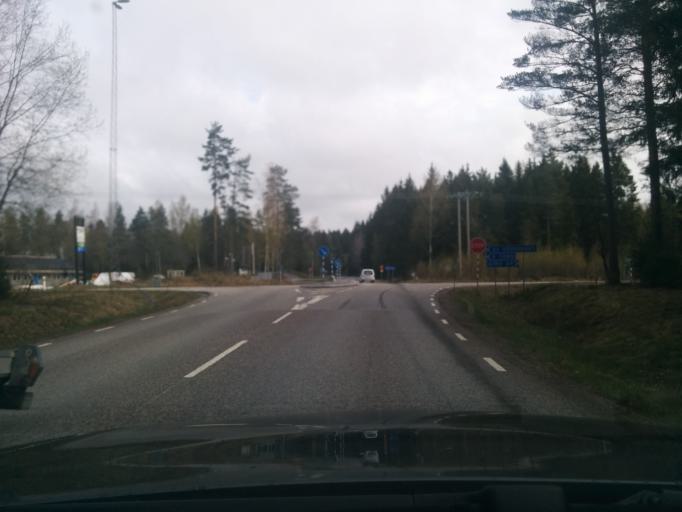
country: SE
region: Uppsala
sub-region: Tierps Kommun
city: Orbyhus
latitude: 60.2162
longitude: 17.7022
